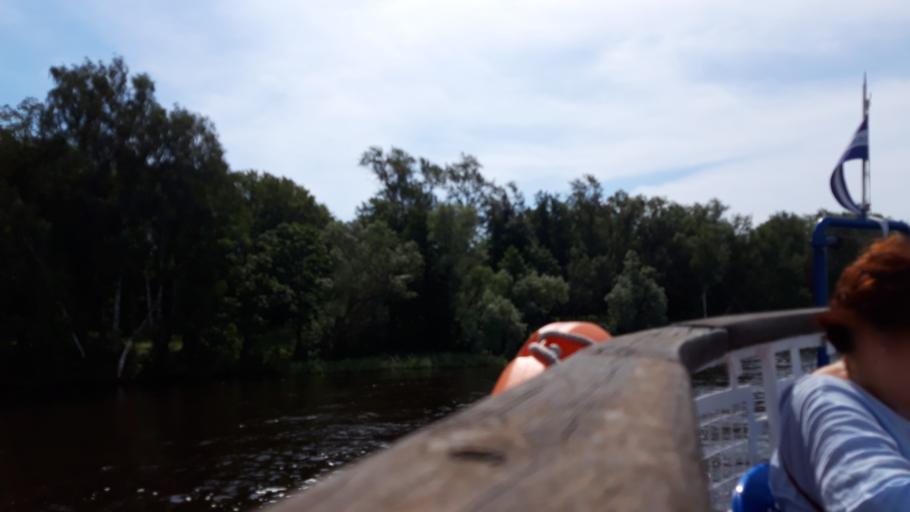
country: RU
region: Tverskaya
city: Konakovo
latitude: 56.6902
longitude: 36.6977
